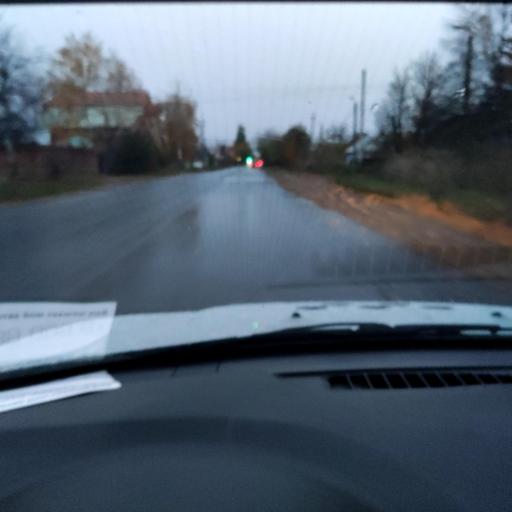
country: RU
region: Samara
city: Tol'yatti
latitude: 53.5392
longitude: 49.4235
